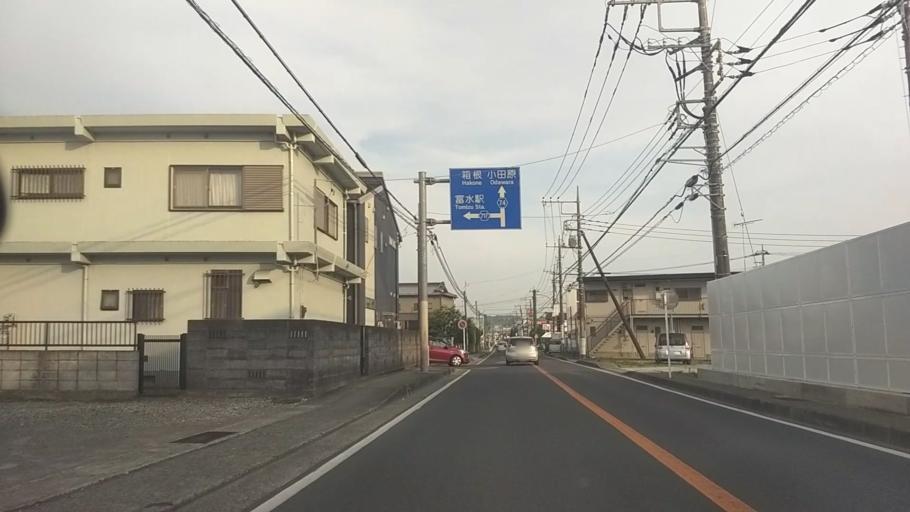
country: JP
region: Kanagawa
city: Odawara
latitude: 35.2953
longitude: 139.1312
